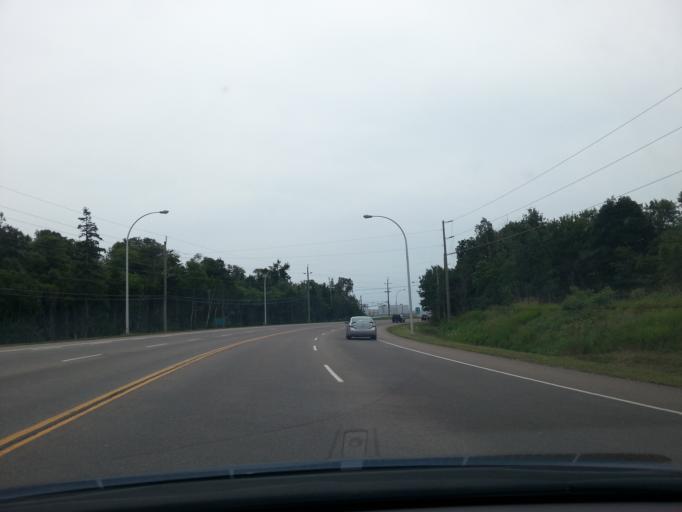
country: CA
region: Prince Edward Island
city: Charlottetown
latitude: 46.2590
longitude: -63.0994
